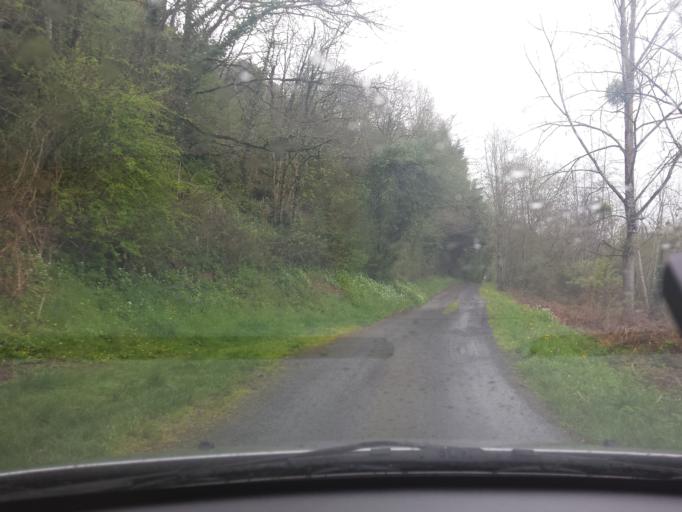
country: FR
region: Pays de la Loire
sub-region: Departement de la Vendee
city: Sainte-Hermine
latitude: 46.5883
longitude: -1.0909
